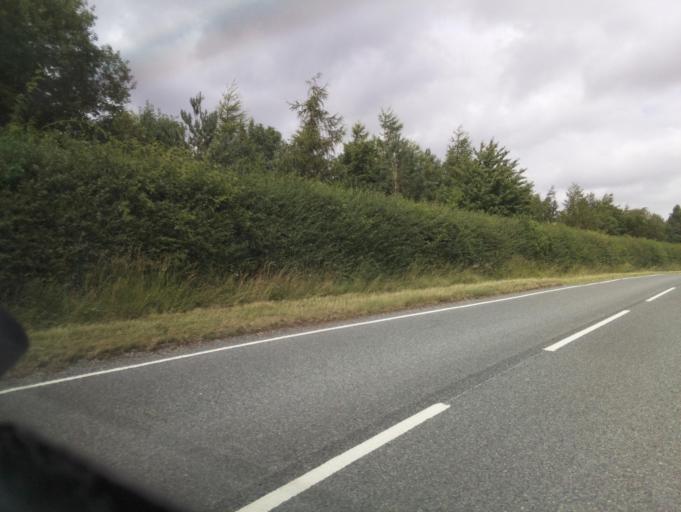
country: GB
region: England
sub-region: District of Rutland
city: Tickencote
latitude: 52.6822
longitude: -0.5035
